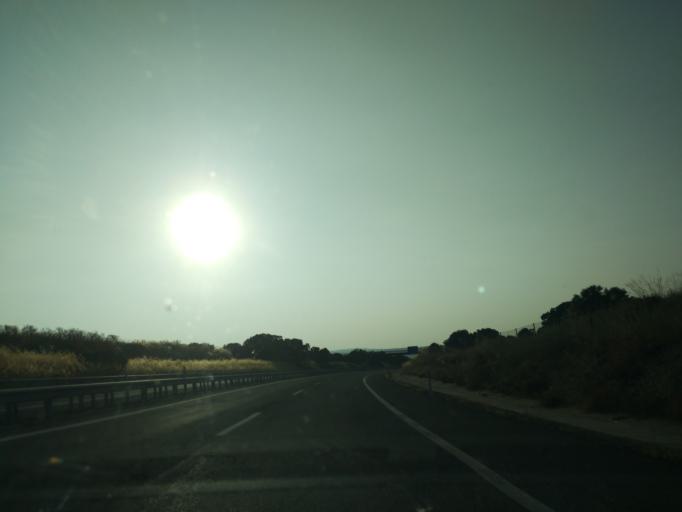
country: ES
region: Castille and Leon
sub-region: Provincia de Avila
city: Avila
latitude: 40.6708
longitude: -4.6730
